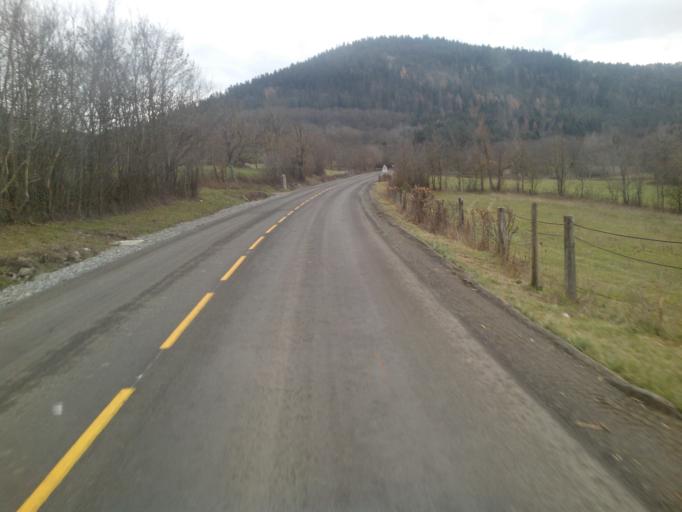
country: FR
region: Languedoc-Roussillon
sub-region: Departement de la Lozere
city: Mende
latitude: 44.4502
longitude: 3.5550
